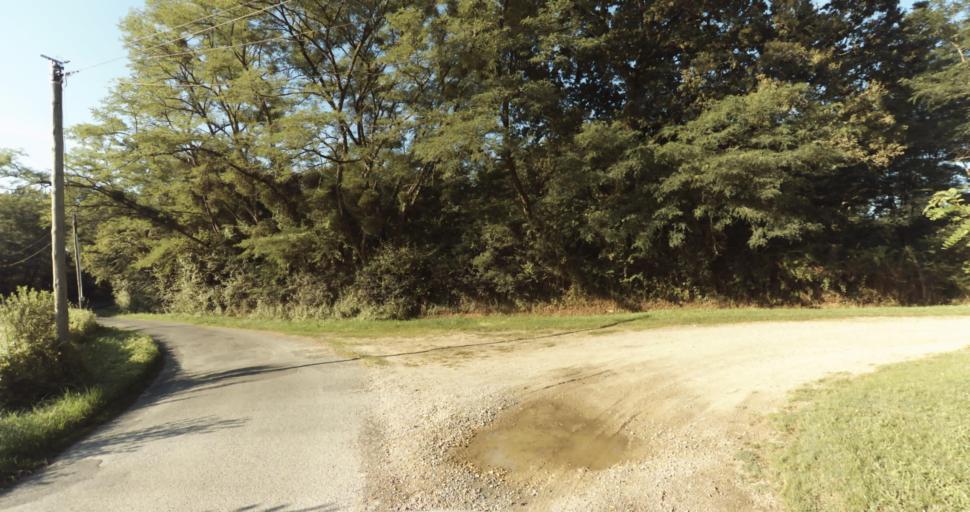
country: FR
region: Aquitaine
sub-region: Departement de la Gironde
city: Bazas
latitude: 44.4047
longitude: -0.2134
